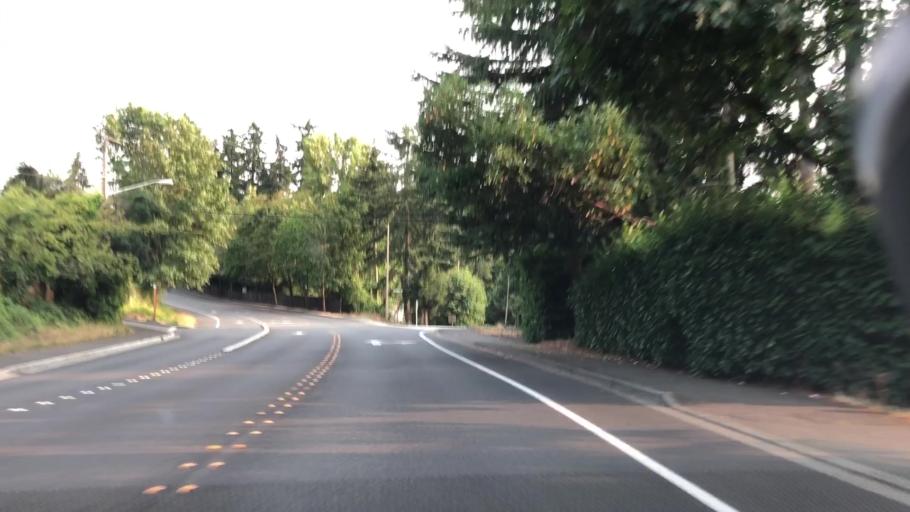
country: US
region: Washington
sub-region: King County
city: Mercer Island
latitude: 47.5678
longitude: -122.2270
